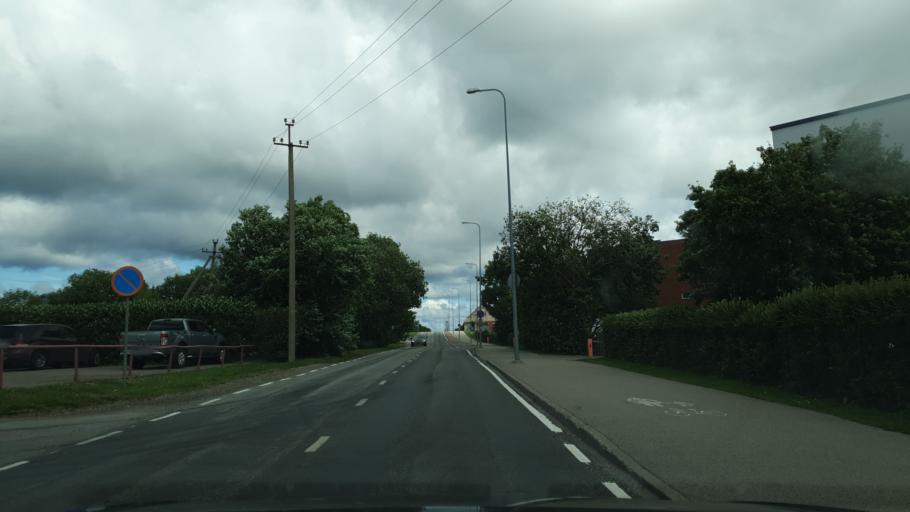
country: EE
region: Harju
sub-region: Viimsi vald
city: Viimsi
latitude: 59.5041
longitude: 24.8405
